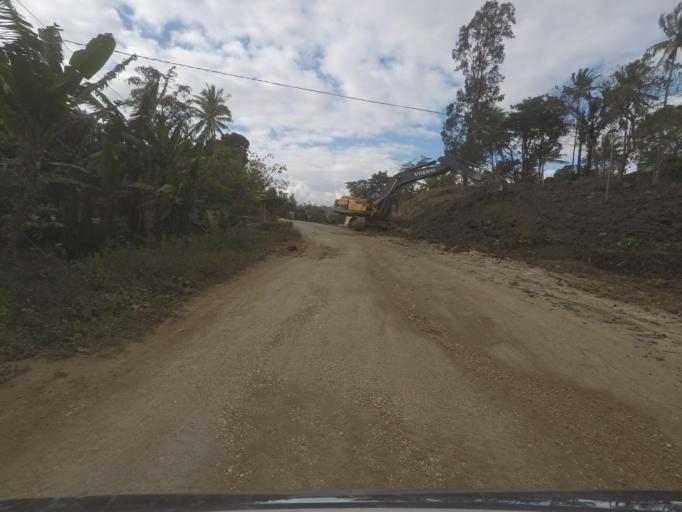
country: TL
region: Baucau
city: Venilale
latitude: -8.6256
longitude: 126.3827
